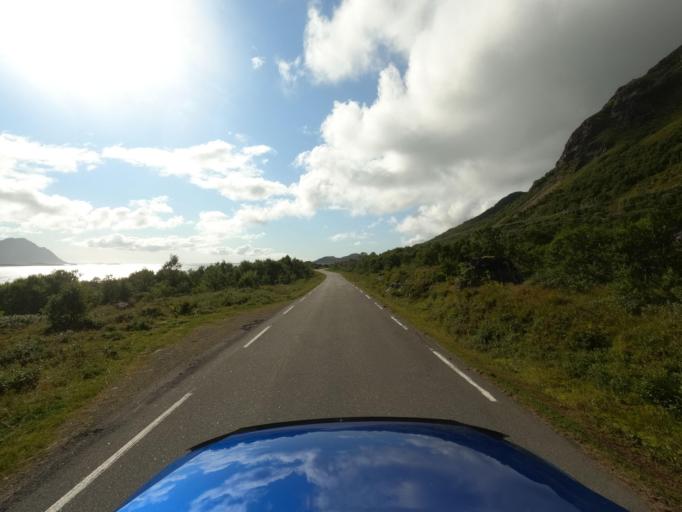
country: NO
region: Nordland
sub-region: Vagan
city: Kabelvag
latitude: 68.2560
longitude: 14.1615
